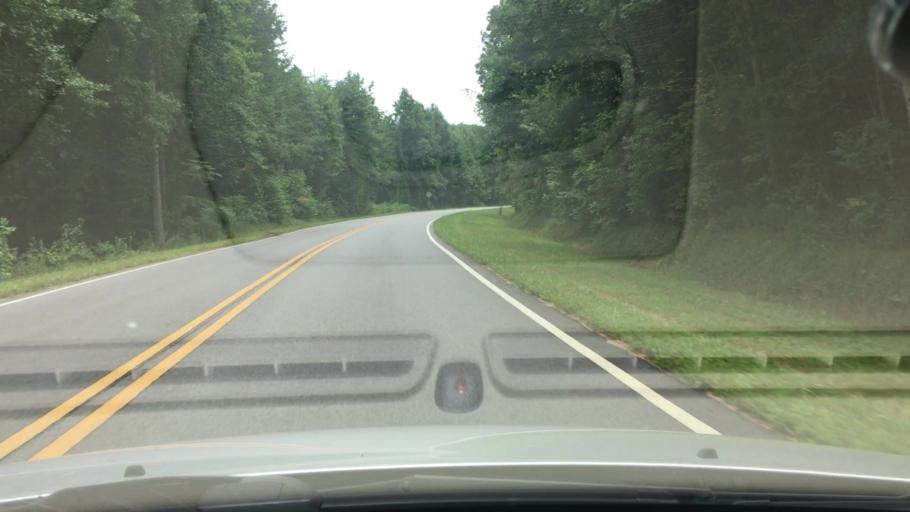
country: US
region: Georgia
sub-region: Lumpkin County
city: Dahlonega
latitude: 34.6247
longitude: -83.8974
